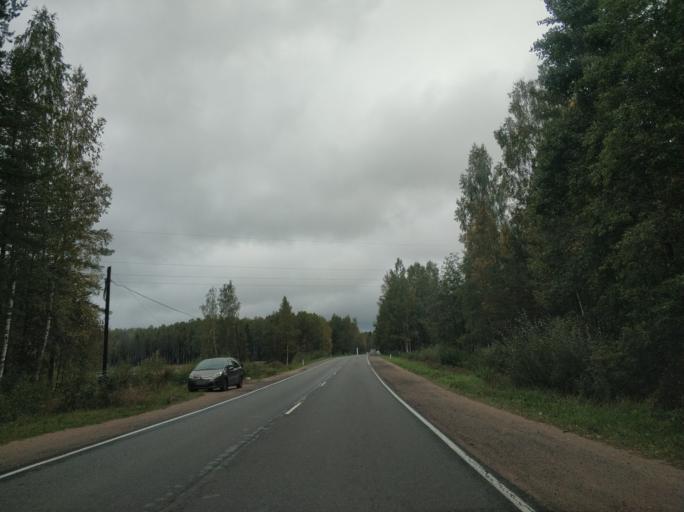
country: RU
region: Leningrad
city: Borisova Griva
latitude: 60.0880
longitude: 30.8698
